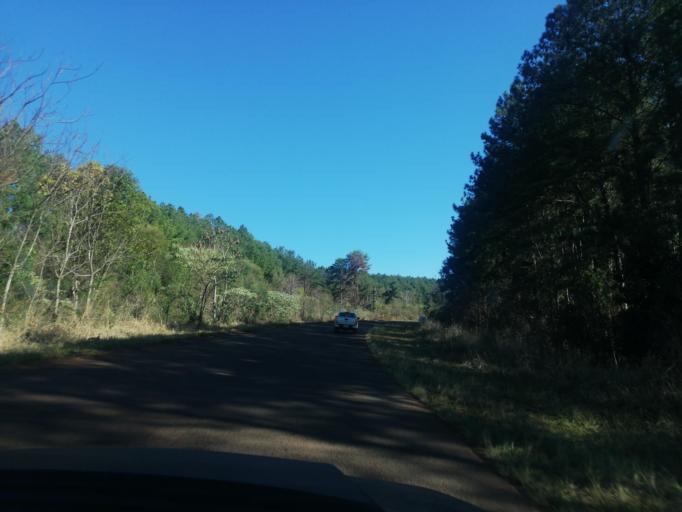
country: AR
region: Misiones
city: Colonia Wanda
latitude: -25.9434
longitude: -54.2904
